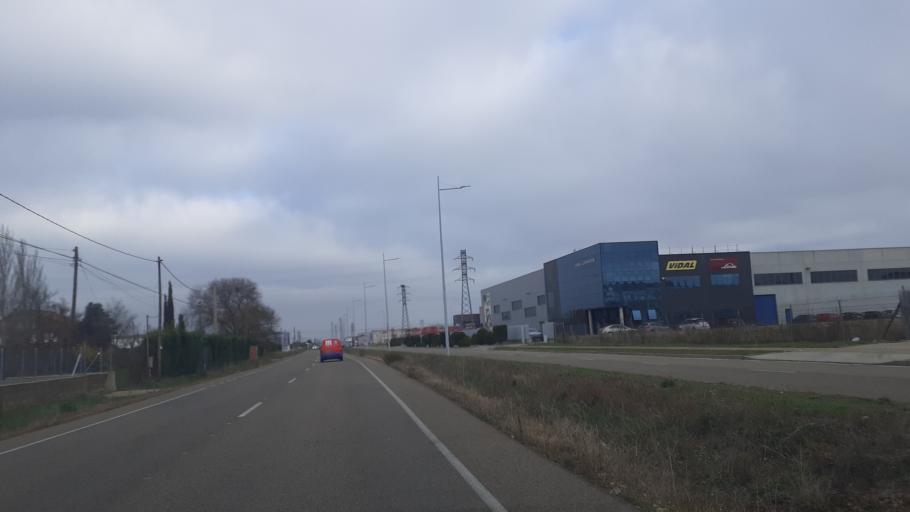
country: ES
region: Castille and Leon
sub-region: Provincia de Leon
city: Onzonilla
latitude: 42.5453
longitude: -5.5876
